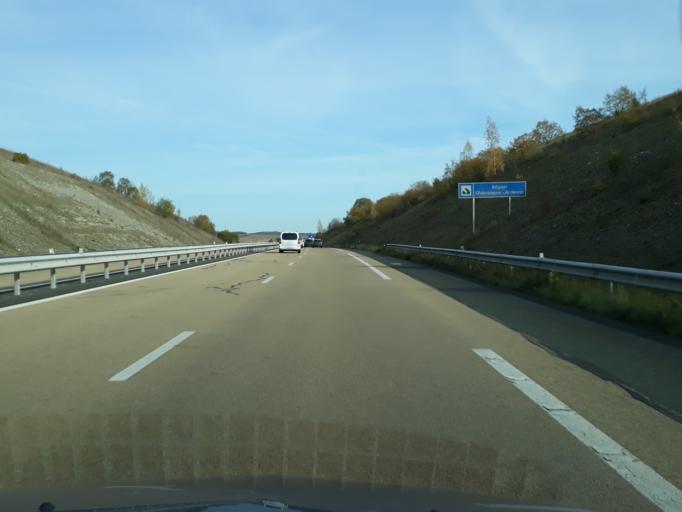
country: FR
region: Champagne-Ardenne
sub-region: Departement de l'Aube
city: Aix-en-Othe
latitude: 48.2462
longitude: 3.6186
